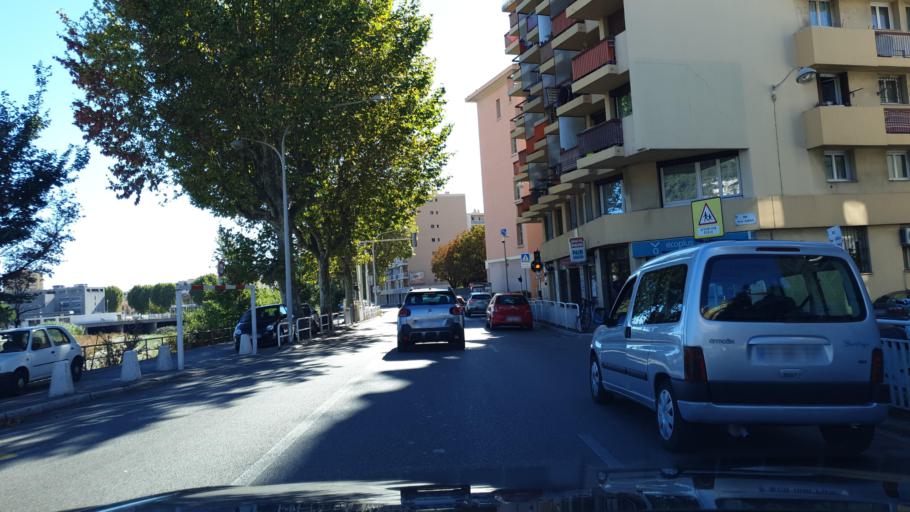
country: FR
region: Provence-Alpes-Cote d'Azur
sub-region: Departement des Alpes-Maritimes
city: Saint-Andre-de-la-Roche
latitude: 43.7193
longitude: 7.2834
